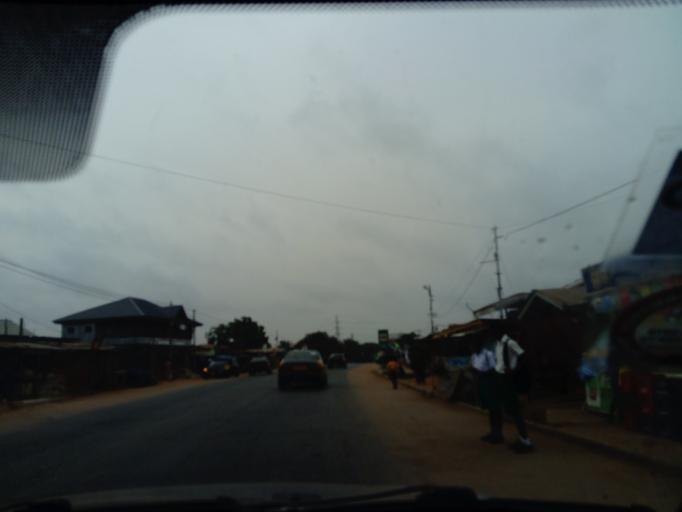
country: GH
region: Central
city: Cape Coast
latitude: 5.1265
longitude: -1.2722
